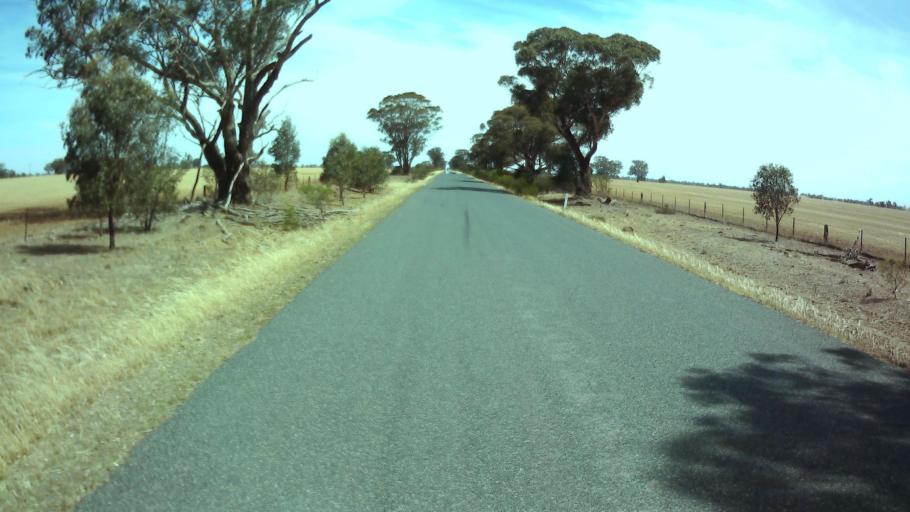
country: AU
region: New South Wales
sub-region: Weddin
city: Grenfell
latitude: -33.9633
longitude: 147.7814
